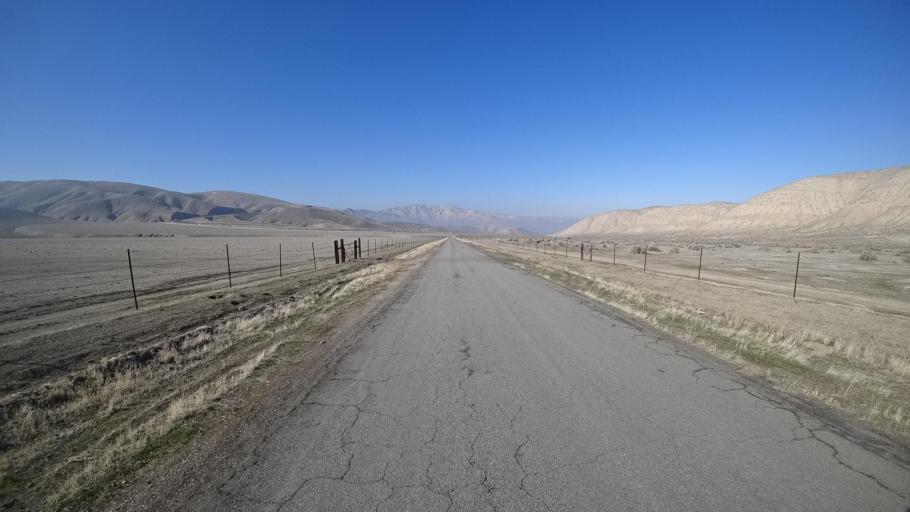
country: US
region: California
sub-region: Kern County
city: Maricopa
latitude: 34.9998
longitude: -119.4016
